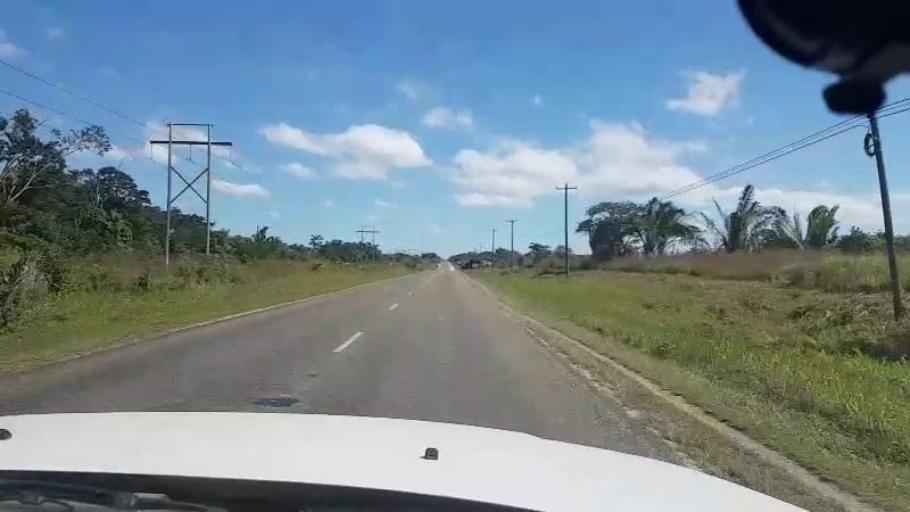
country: BZ
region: Cayo
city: Belmopan
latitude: 17.2768
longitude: -88.7245
